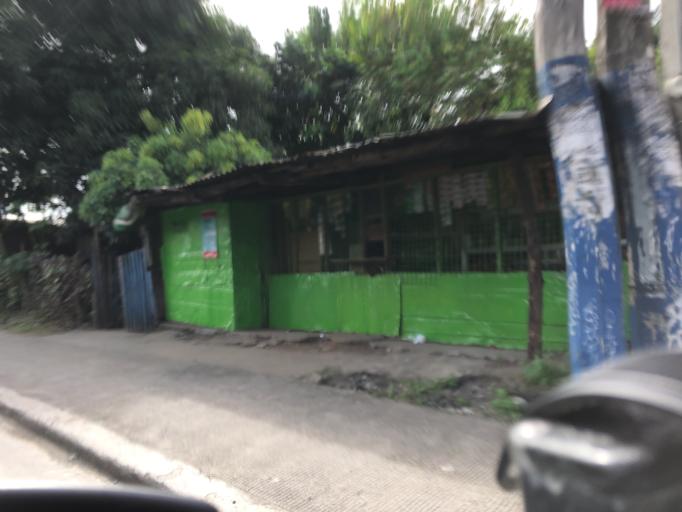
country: PH
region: Calabarzon
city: Bagong Pagasa
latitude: 14.7184
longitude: 121.0612
